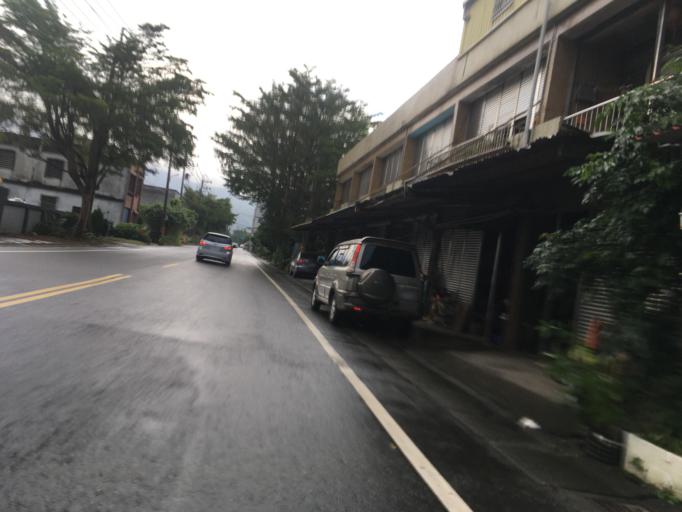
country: TW
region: Taiwan
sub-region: Yilan
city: Yilan
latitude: 24.8313
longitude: 121.8026
